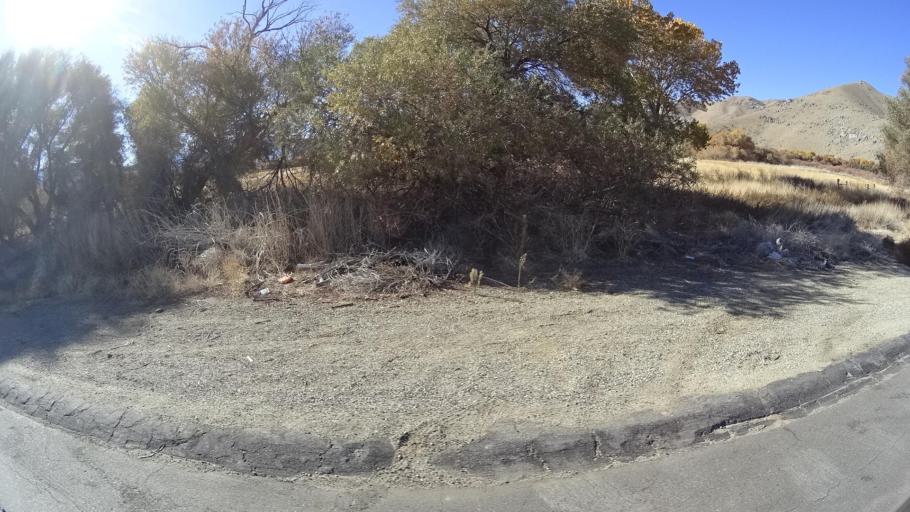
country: US
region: California
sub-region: Kern County
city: Weldon
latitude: 35.6666
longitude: -118.3227
